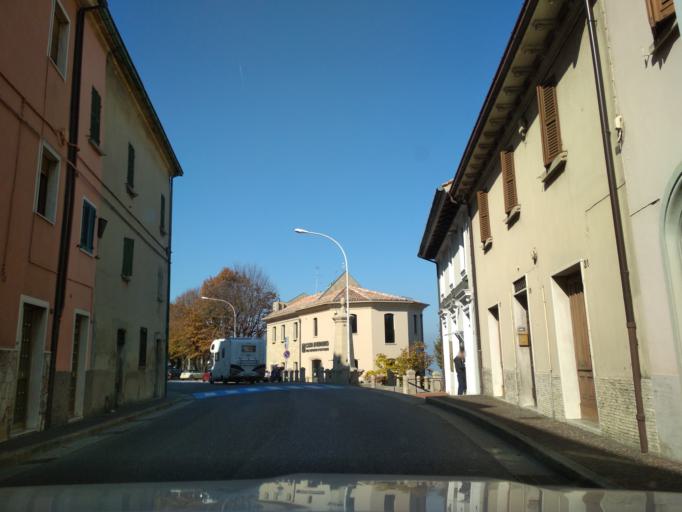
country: SM
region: Borgo Maggiore
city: Borgo Maggiore
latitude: 43.9396
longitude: 12.4477
